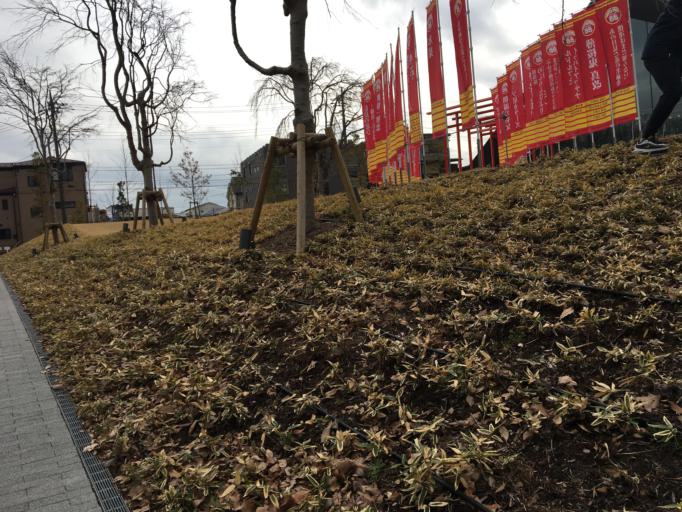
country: JP
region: Saitama
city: Tokorozawa
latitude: 35.7975
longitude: 139.5087
